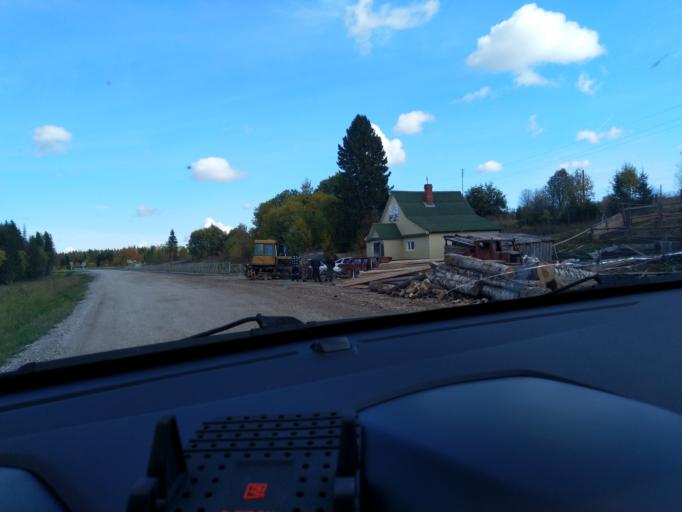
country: RU
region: Perm
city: Usol'ye
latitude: 59.4622
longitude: 56.3637
